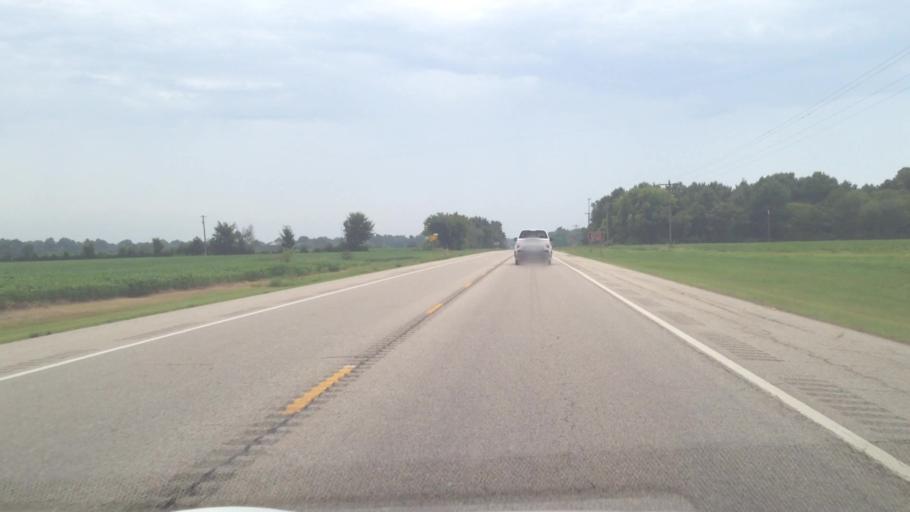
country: US
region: Kansas
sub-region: Cherokee County
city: Galena
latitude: 37.1947
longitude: -94.7047
